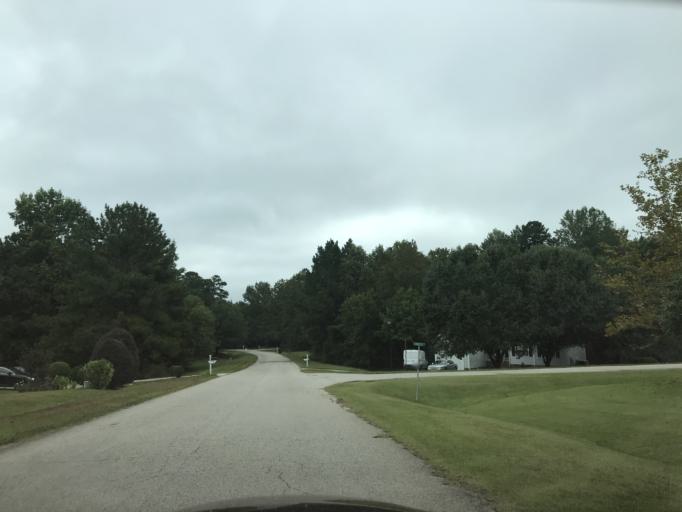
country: US
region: North Carolina
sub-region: Wake County
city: Rolesville
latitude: 35.9698
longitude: -78.3644
